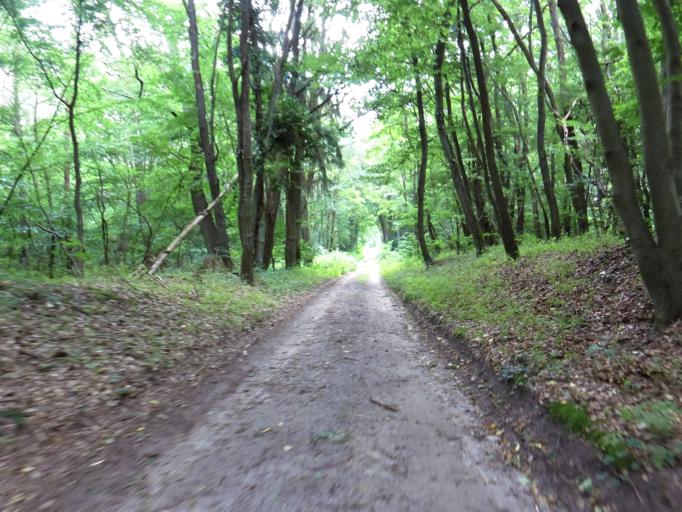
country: DE
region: Brandenburg
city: Lychen
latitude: 53.2151
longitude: 13.2926
